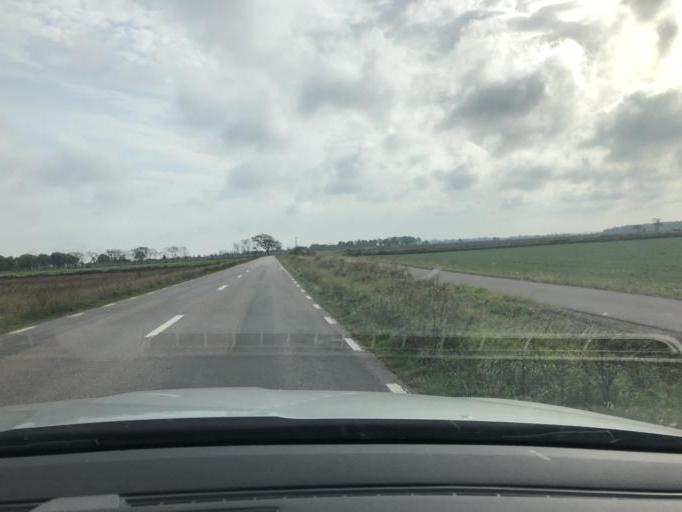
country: SE
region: Kalmar
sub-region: Morbylanga Kommun
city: Moerbylanga
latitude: 56.3072
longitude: 16.4095
